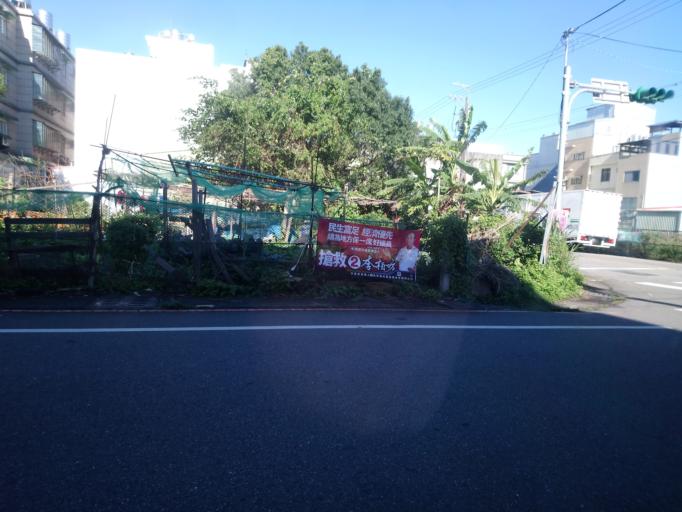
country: TW
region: Taiwan
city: Daxi
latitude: 24.9043
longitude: 121.2777
